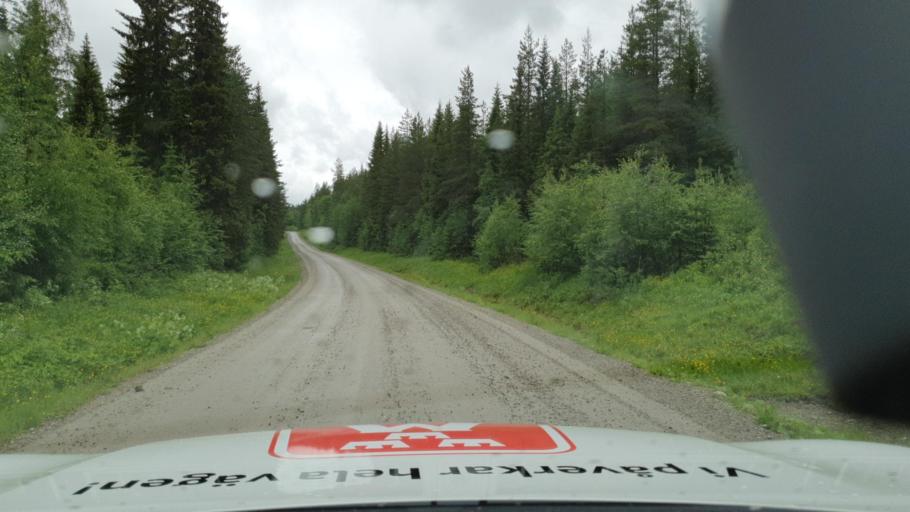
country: SE
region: Vaesterbotten
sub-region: Dorotea Kommun
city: Dorotea
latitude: 64.0489
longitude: 16.7314
